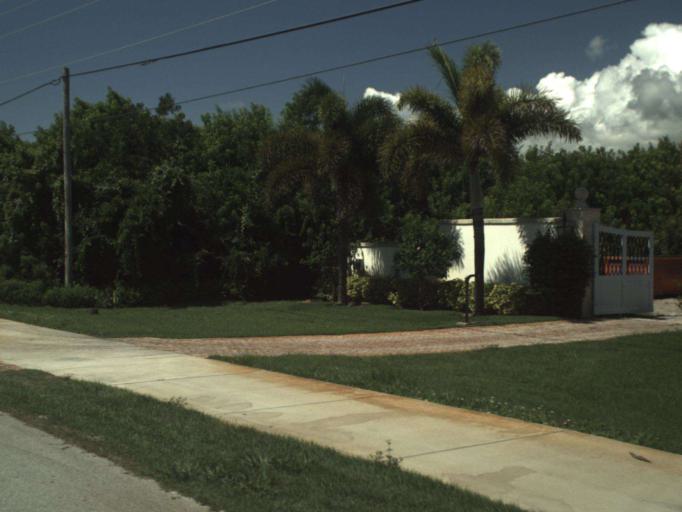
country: US
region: Florida
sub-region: Indian River County
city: South Beach
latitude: 27.5677
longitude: -80.3272
